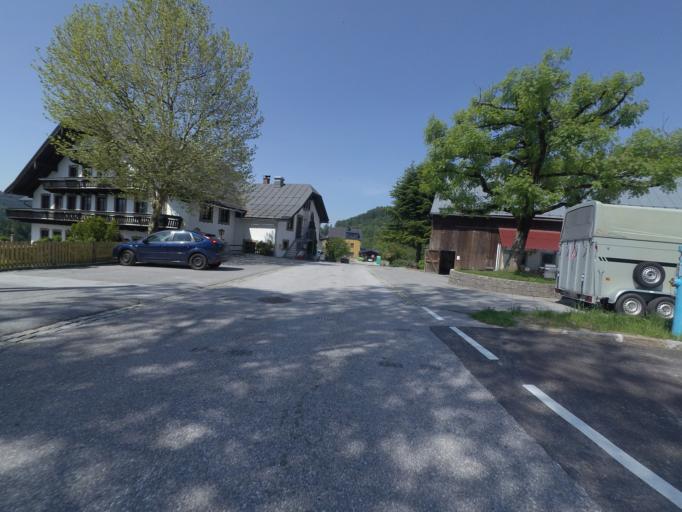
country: AT
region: Salzburg
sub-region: Politischer Bezirk Salzburg-Umgebung
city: Koppl
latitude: 47.7765
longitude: 13.1223
